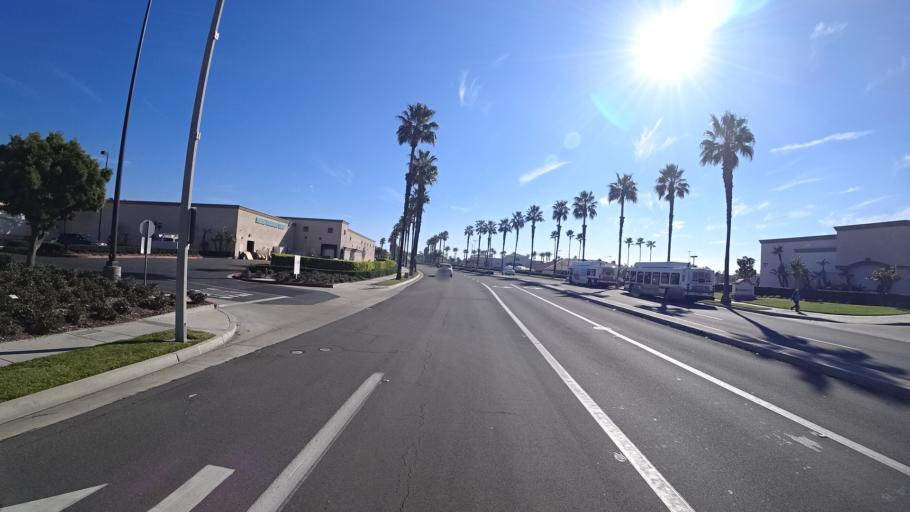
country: US
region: California
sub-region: Orange County
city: Foothill Ranch
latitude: 33.6816
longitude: -117.6687
